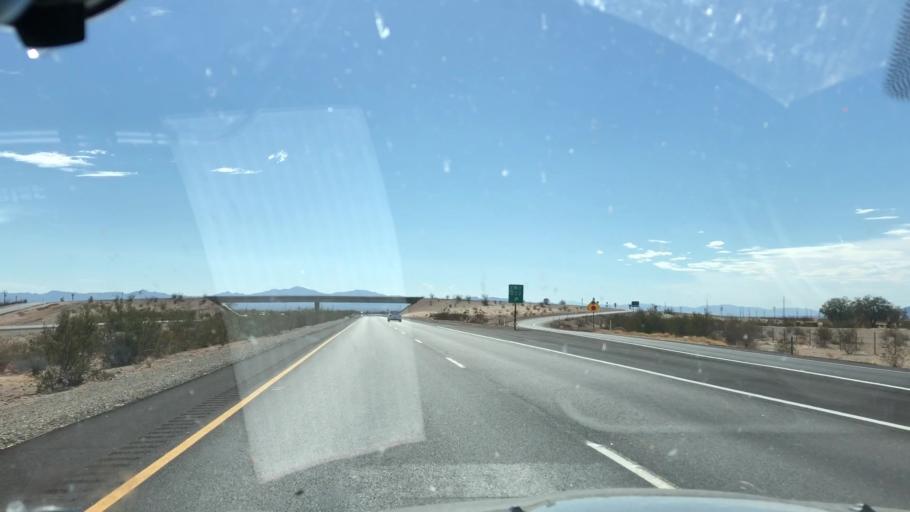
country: US
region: California
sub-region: Riverside County
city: Mesa Verde
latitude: 33.6082
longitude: -114.8979
